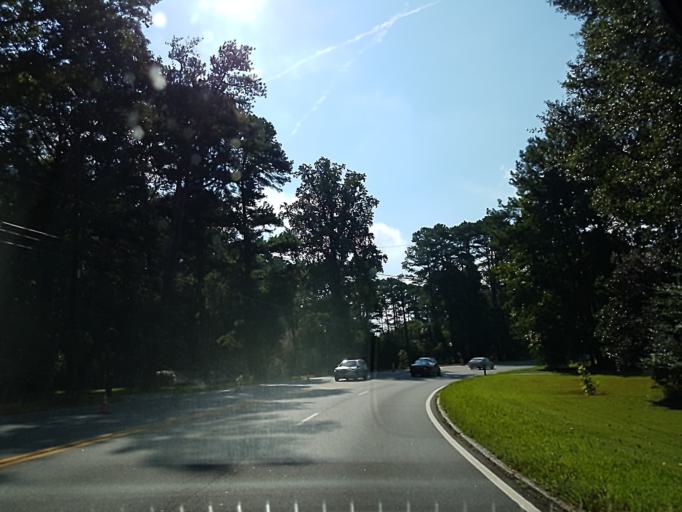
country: US
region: Georgia
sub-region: DeKalb County
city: North Druid Hills
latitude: 33.8213
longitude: -84.3048
